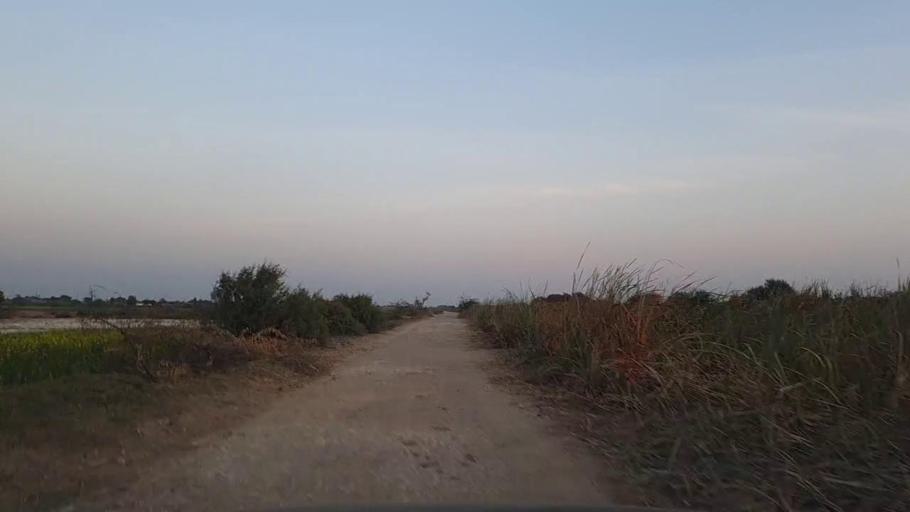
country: PK
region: Sindh
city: Tando Mittha Khan
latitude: 25.9421
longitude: 69.1370
